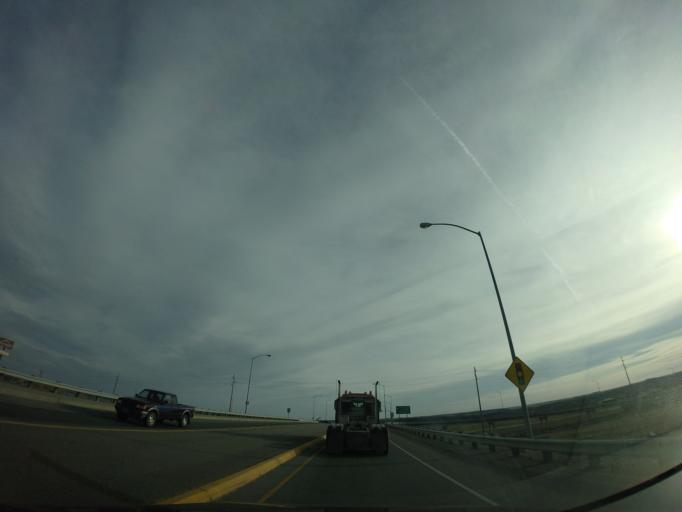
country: US
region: Montana
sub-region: Yellowstone County
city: Billings
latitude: 45.7334
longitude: -108.6050
